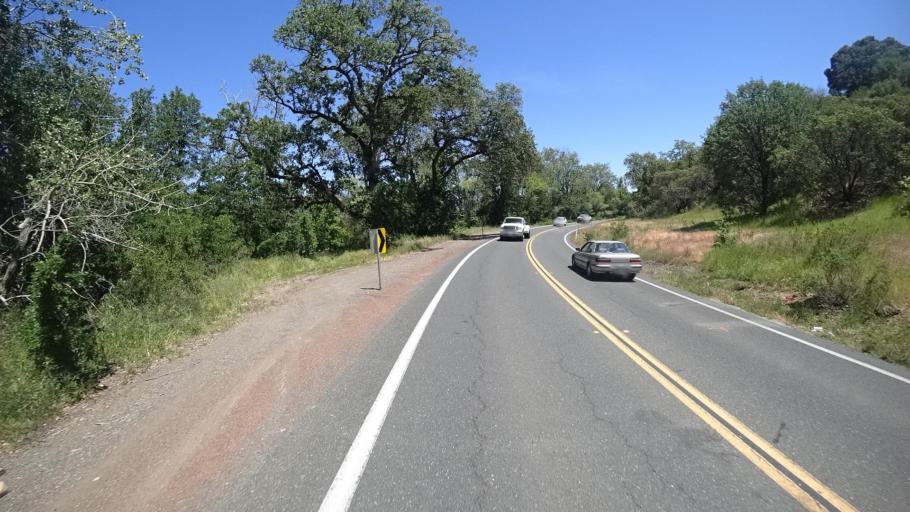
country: US
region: California
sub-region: Lake County
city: North Lakeport
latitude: 39.1211
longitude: -122.8912
